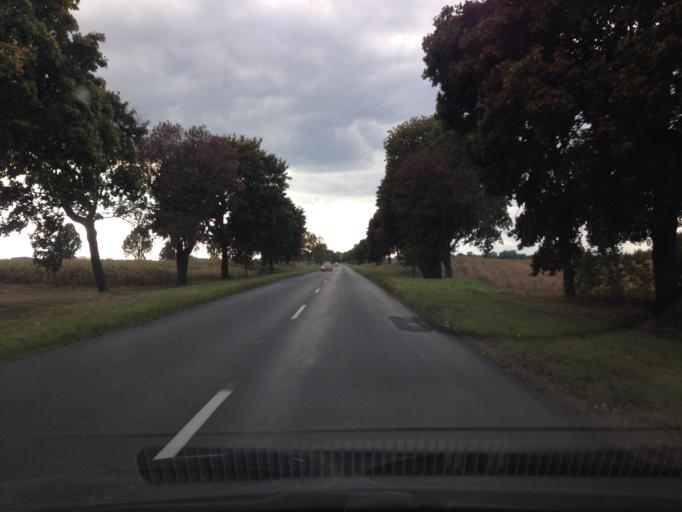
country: PL
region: Kujawsko-Pomorskie
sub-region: Powiat lipnowski
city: Chrostkowo
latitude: 52.9360
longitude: 19.2727
